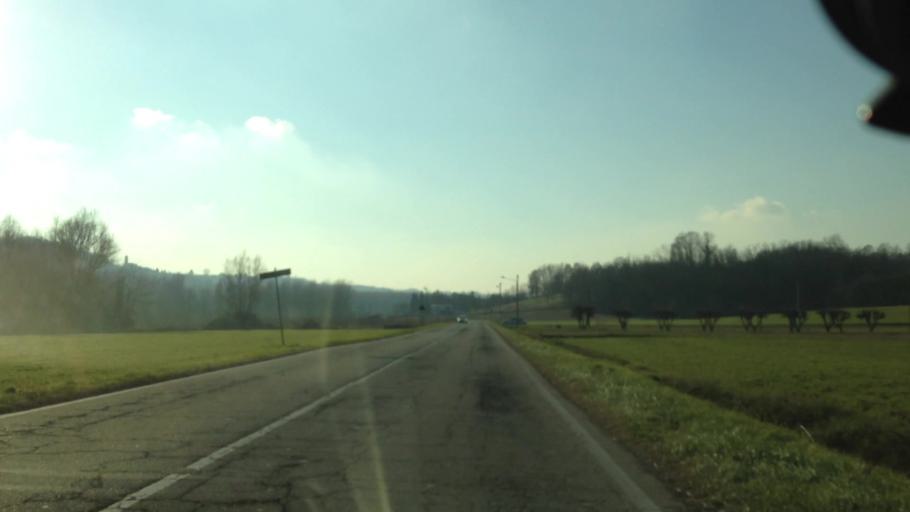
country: IT
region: Piedmont
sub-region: Provincia di Asti
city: Cortiglione
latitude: 44.8347
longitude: 8.3743
